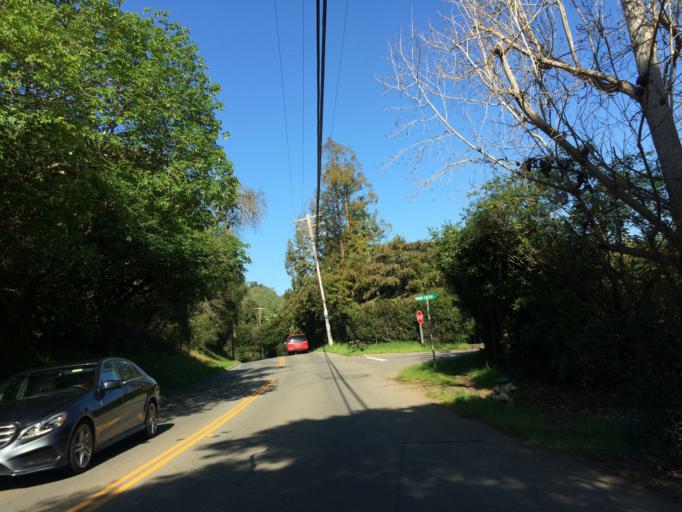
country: US
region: California
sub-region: Santa Clara County
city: Los Altos Hills
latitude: 37.3800
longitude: -122.1636
